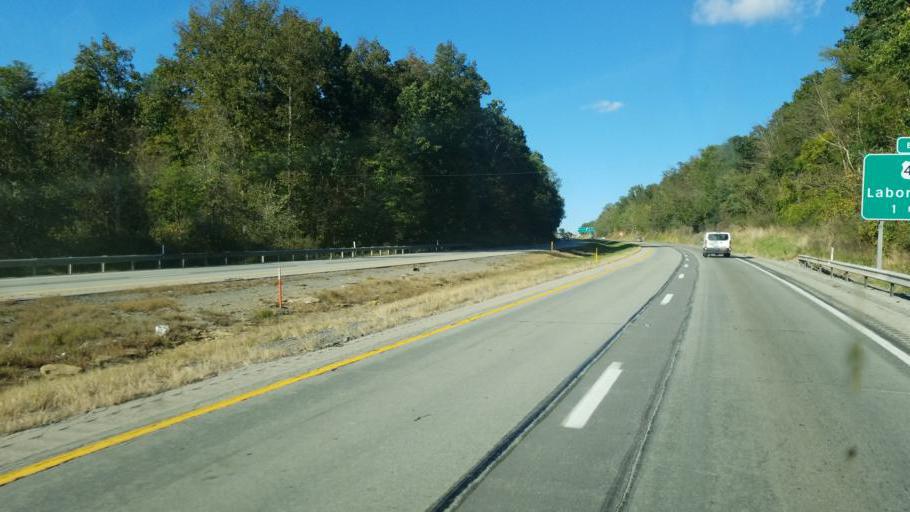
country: US
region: Pennsylvania
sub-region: Washington County
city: East Washington
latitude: 40.1355
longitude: -80.2074
